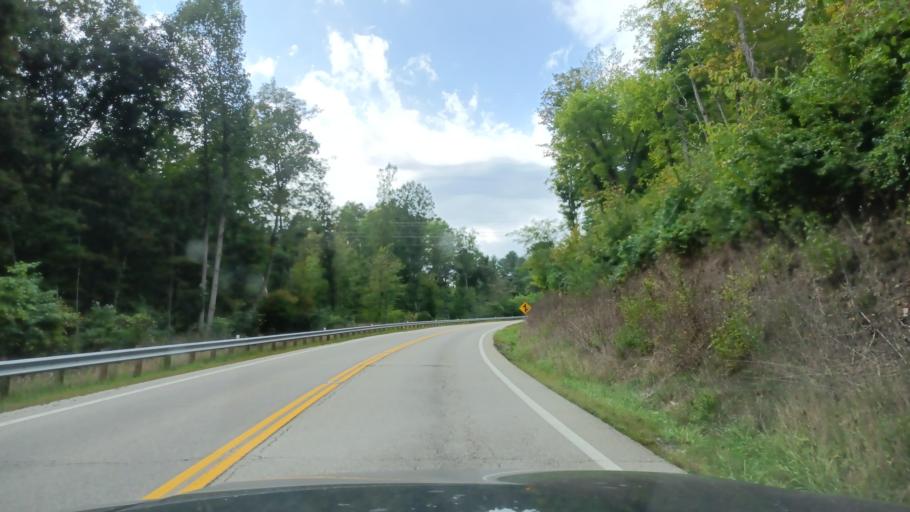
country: US
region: Ohio
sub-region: Vinton County
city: McArthur
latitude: 39.2363
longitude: -82.3397
